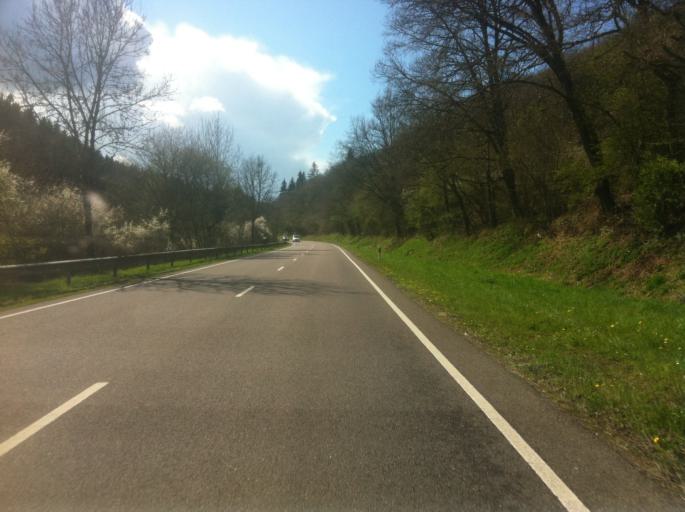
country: LU
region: Diekirch
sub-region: Canton de Wiltz
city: Esch-sur-Sure
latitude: 49.9330
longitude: 5.9277
